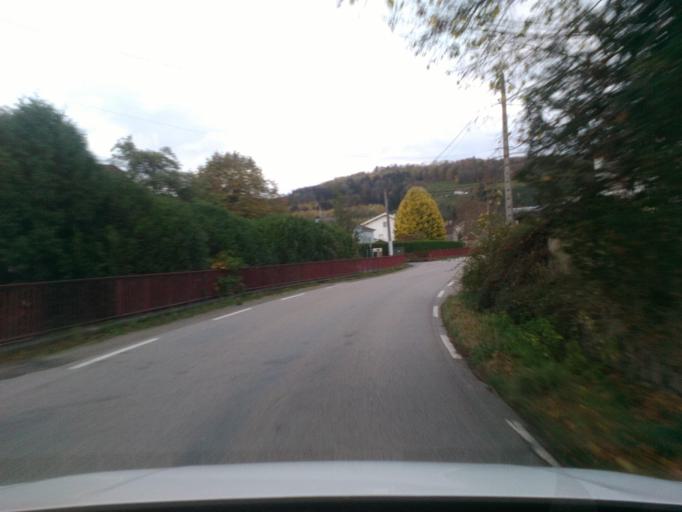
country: FR
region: Lorraine
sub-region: Departement des Vosges
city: Ban-de-Laveline
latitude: 48.2329
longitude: 7.0616
